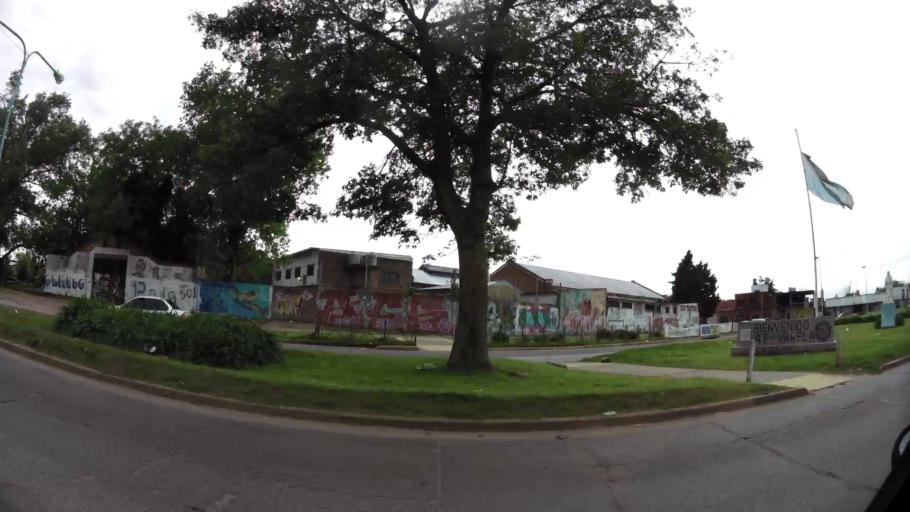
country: AR
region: Buenos Aires
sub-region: Partido de Quilmes
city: Quilmes
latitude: -34.7886
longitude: -58.2789
